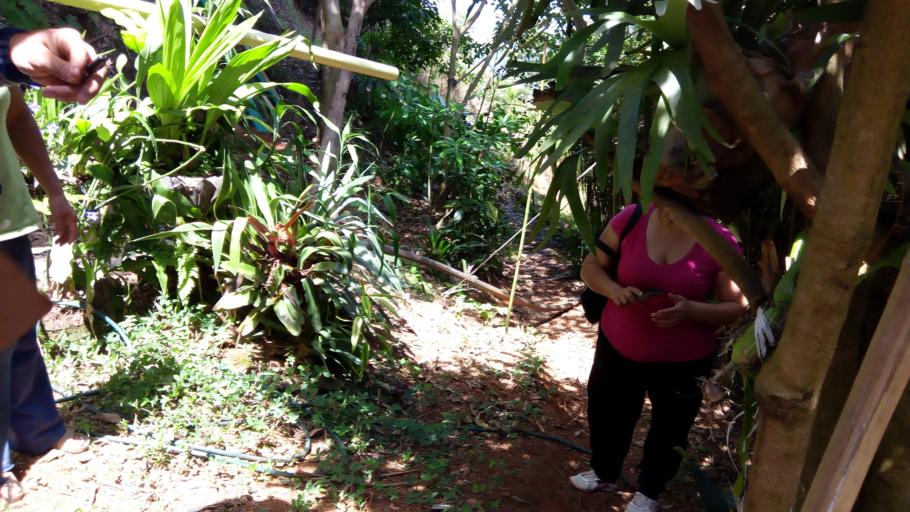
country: CO
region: Valle del Cauca
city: Cali
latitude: 3.4396
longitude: -76.5916
